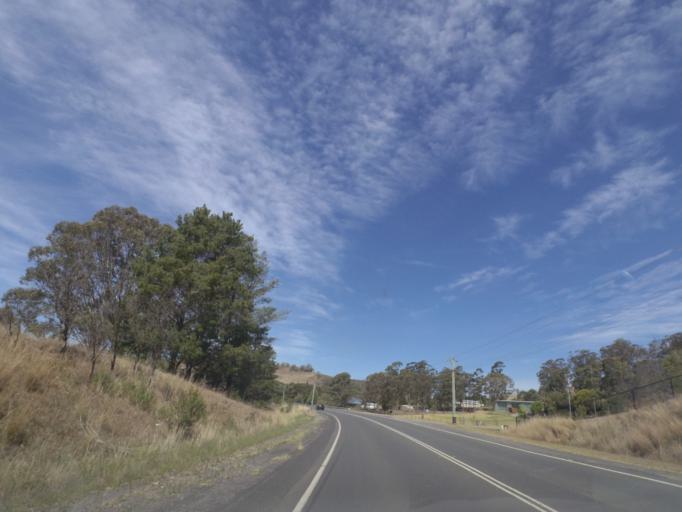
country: AU
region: New South Wales
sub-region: Wollondilly
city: Picton
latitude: -34.1671
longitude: 150.6242
